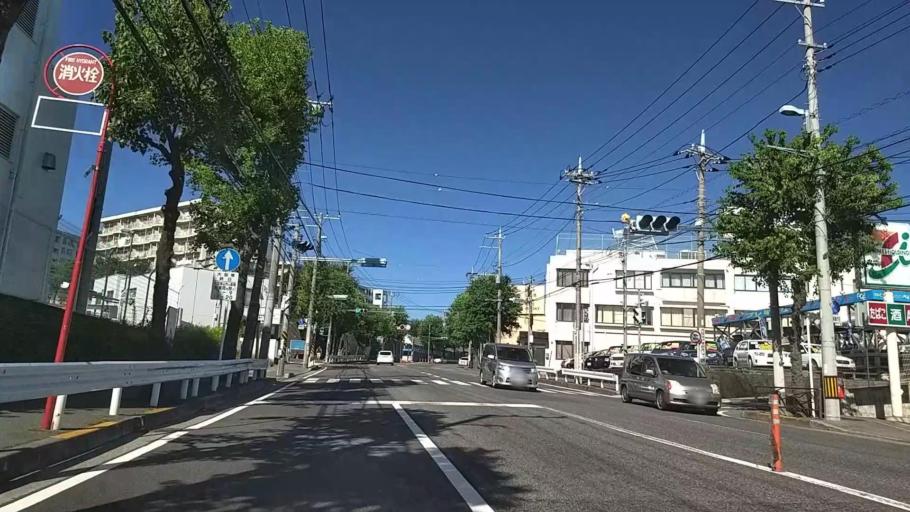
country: JP
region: Tokyo
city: Chofugaoka
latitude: 35.5887
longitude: 139.5593
